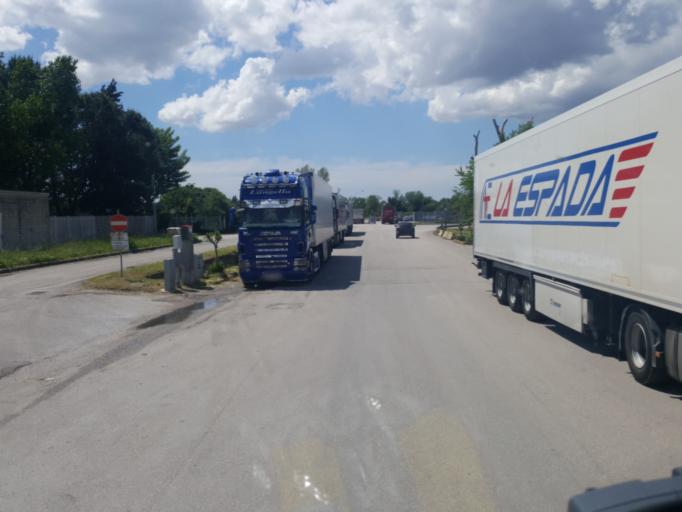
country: IT
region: Campania
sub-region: Provincia di Napoli
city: Pascarola
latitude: 40.9827
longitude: 14.3011
